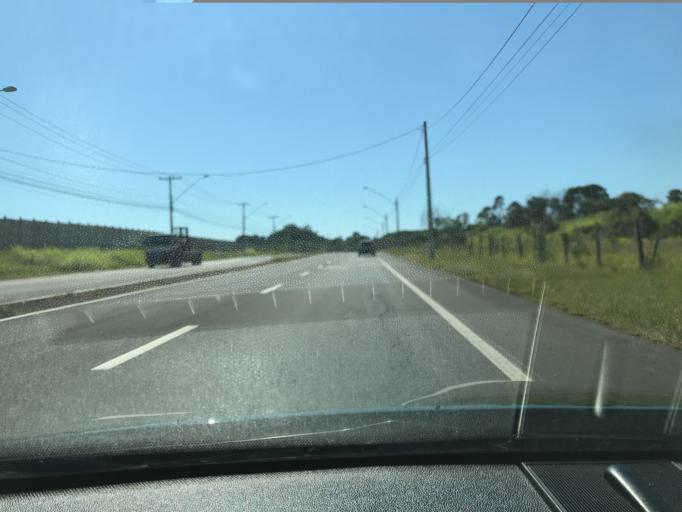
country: BR
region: Sao Paulo
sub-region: Campinas
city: Campinas
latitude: -22.8727
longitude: -47.0900
